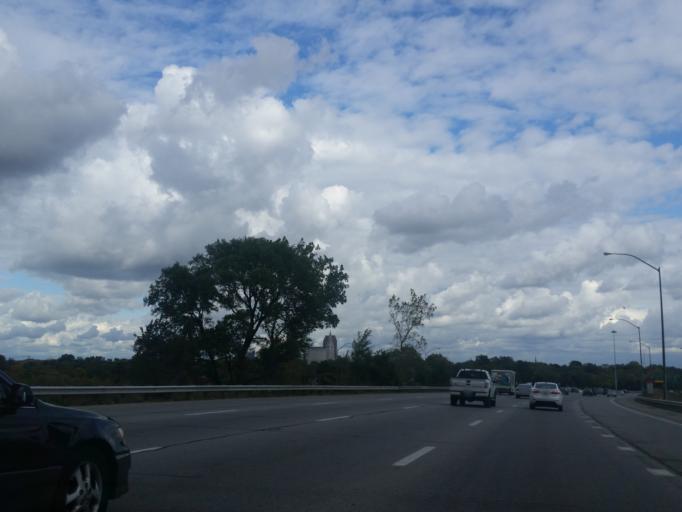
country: US
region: Ohio
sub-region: Cuyahoga County
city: Brooklyn
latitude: 41.4734
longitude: -81.7259
